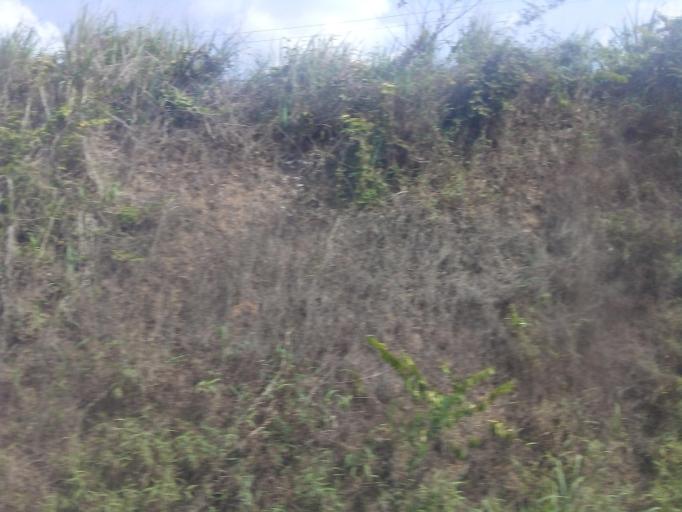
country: BR
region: Maranhao
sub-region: Santa Ines
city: Santa Ines
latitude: -3.9467
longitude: -46.2241
